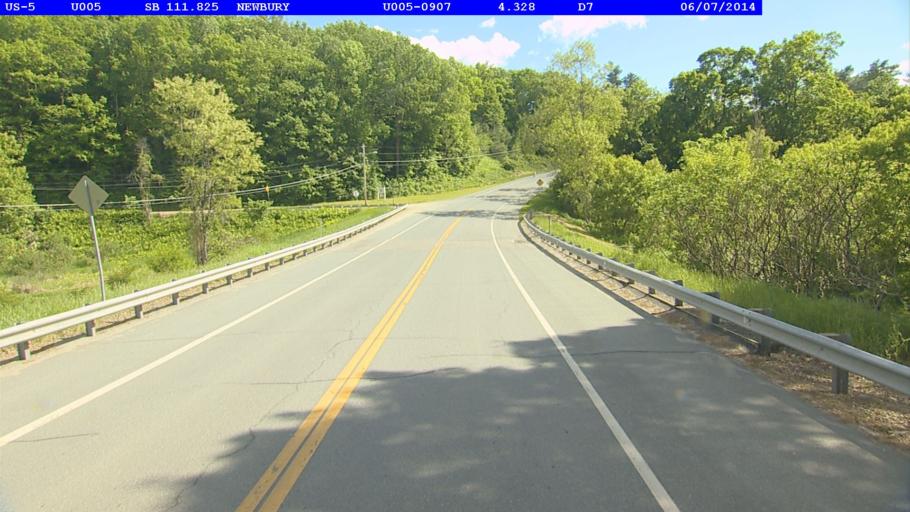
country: US
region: New Hampshire
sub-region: Grafton County
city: North Haverhill
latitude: 44.0853
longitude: -72.0510
